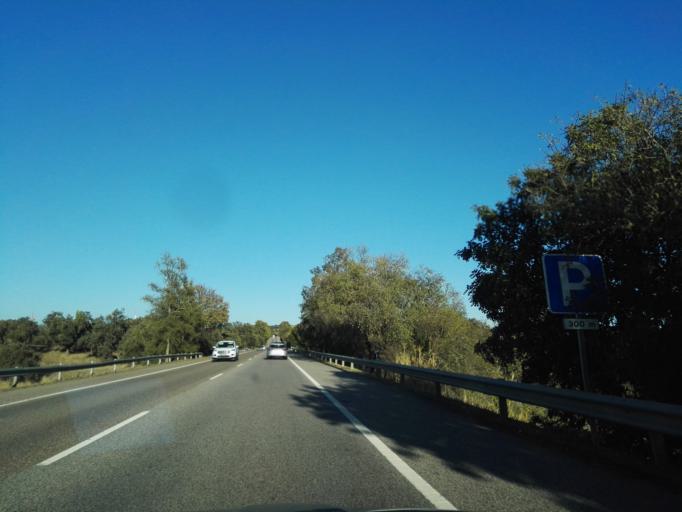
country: PT
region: Evora
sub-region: Vila Vicosa
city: Vila Vicosa
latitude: 38.8565
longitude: -7.3147
